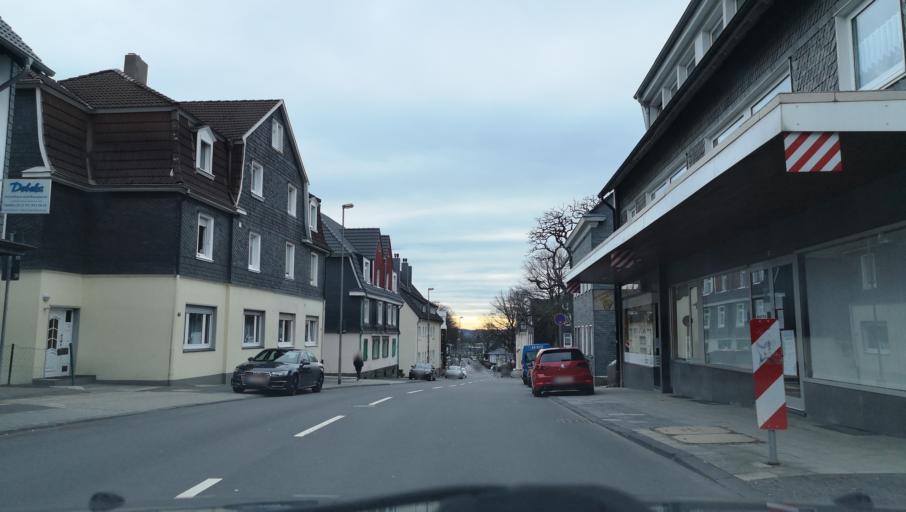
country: DE
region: North Rhine-Westphalia
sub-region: Regierungsbezirk Dusseldorf
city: Remscheid
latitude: 51.2098
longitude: 7.2341
